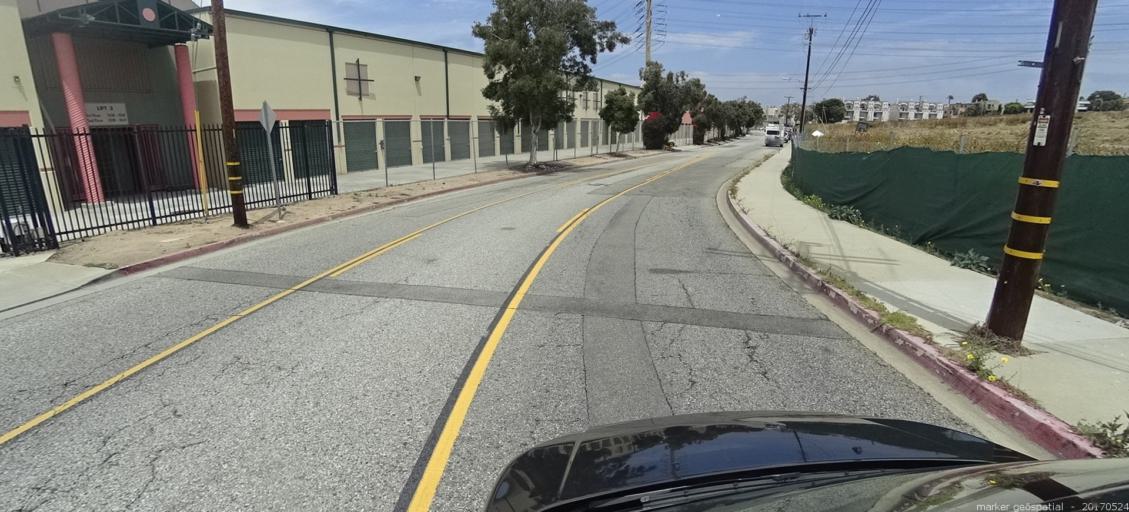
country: US
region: California
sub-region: Los Angeles County
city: Redondo Beach
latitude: 33.8517
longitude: -118.3925
